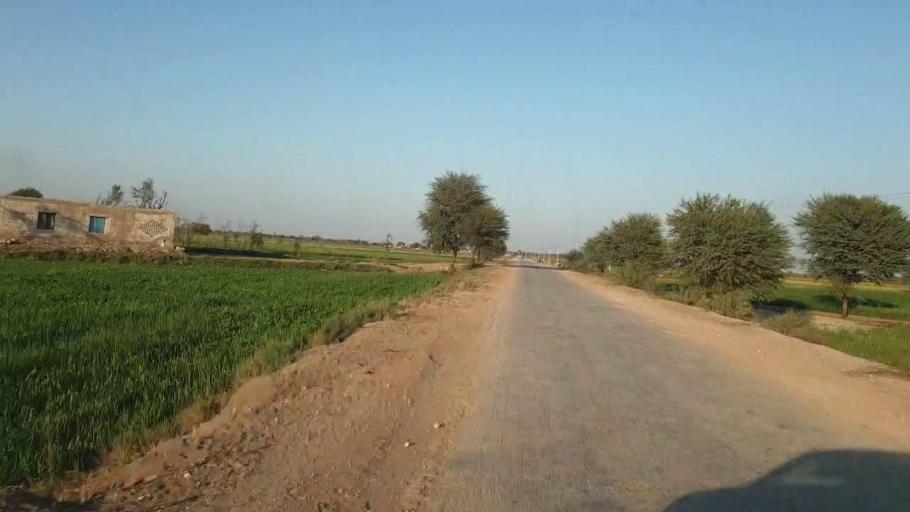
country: PK
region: Sindh
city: Tando Allahyar
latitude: 25.3793
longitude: 68.7498
